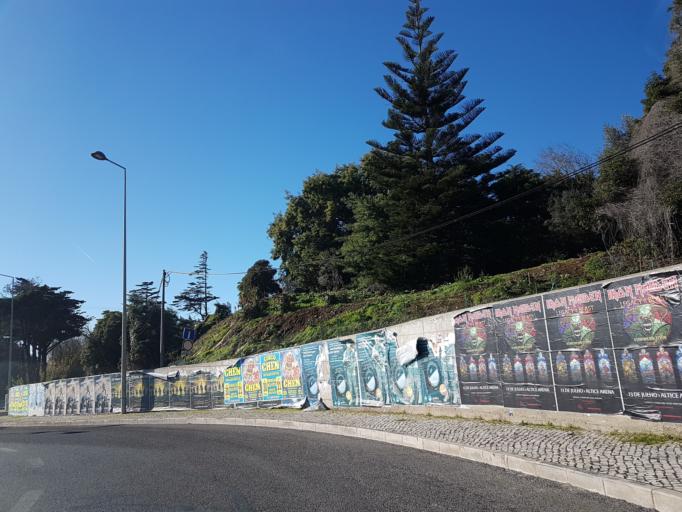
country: PT
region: Lisbon
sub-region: Sintra
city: Sintra
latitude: 38.7820
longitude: -9.3765
